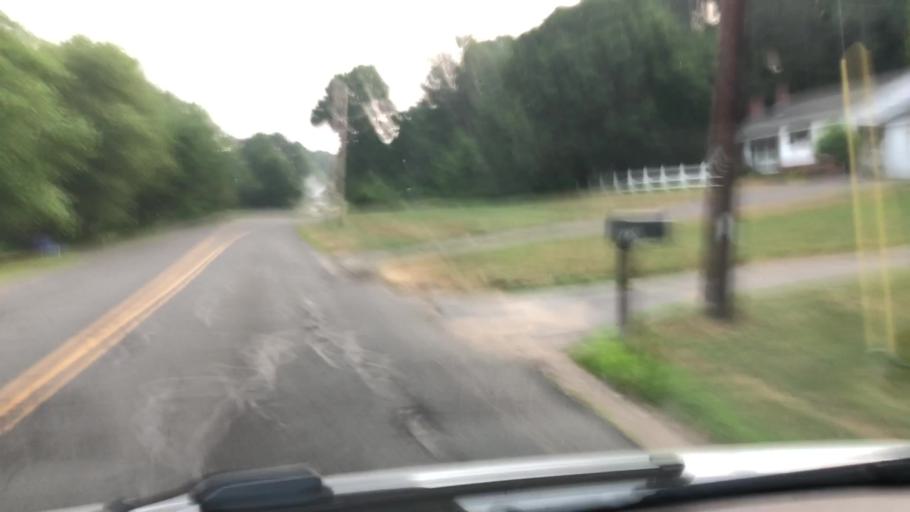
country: US
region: Massachusetts
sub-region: Hampshire County
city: Easthampton
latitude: 42.2904
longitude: -72.6721
